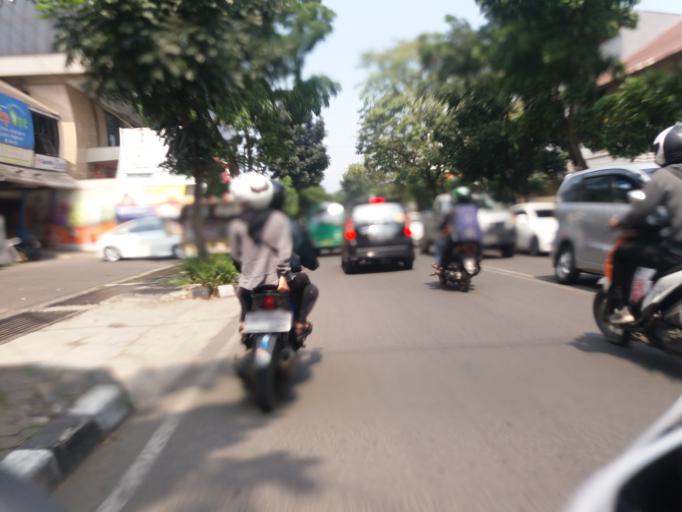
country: ID
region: West Java
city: Bandung
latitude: -6.9121
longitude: 107.5780
